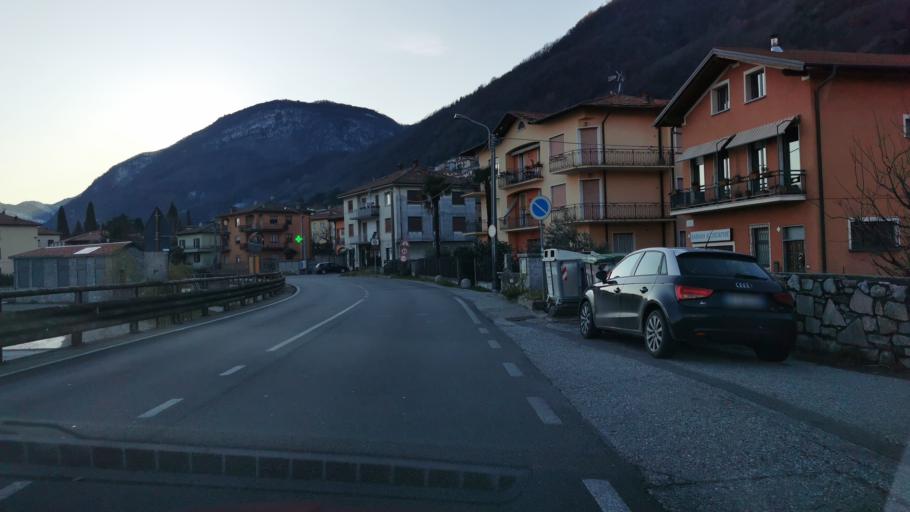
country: IT
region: Lombardy
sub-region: Provincia di Como
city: San Siro
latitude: 46.0659
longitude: 9.2704
